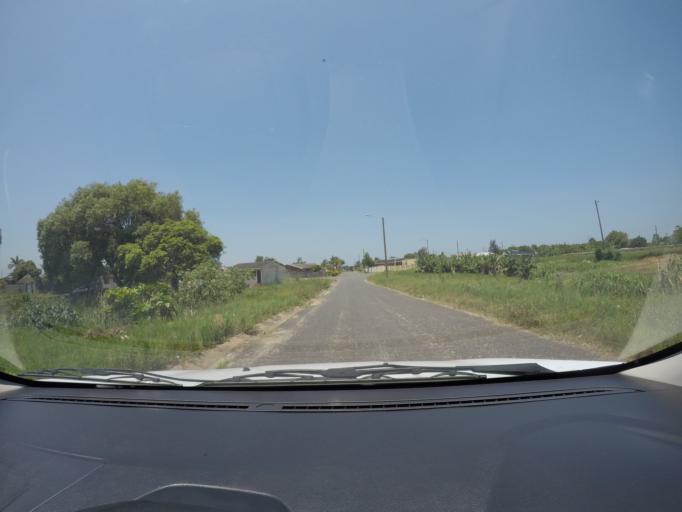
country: ZA
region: KwaZulu-Natal
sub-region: uThungulu District Municipality
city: eSikhawini
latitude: -28.8920
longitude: 31.8844
